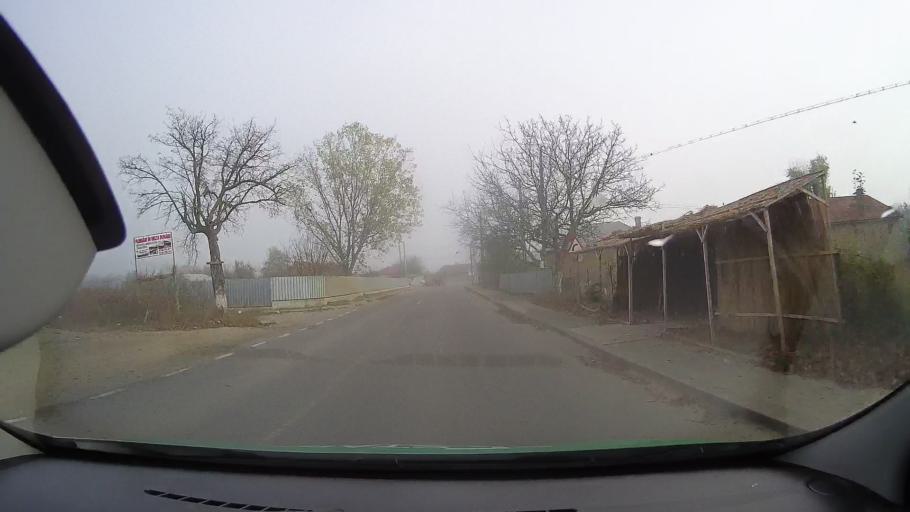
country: RO
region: Tulcea
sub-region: Comuna Nufaru
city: Nufaru
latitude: 45.1494
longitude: 28.9145
